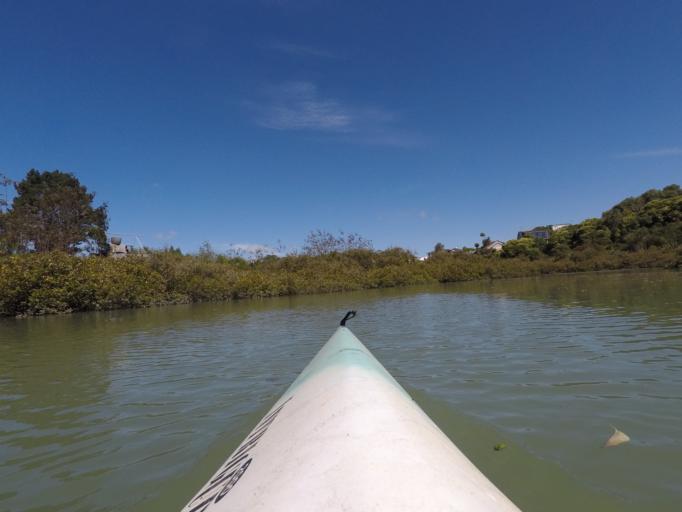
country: NZ
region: Auckland
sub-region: Auckland
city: Rosebank
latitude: -36.8725
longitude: 174.6992
